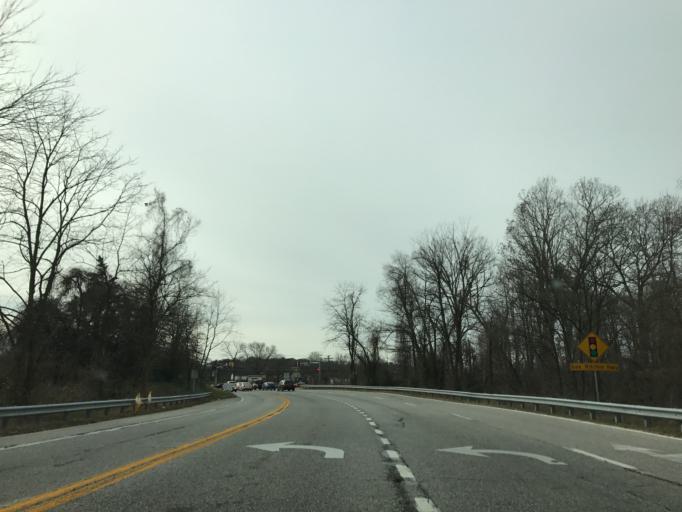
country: US
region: Maryland
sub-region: Anne Arundel County
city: Severna Park
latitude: 39.0870
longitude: -76.5523
